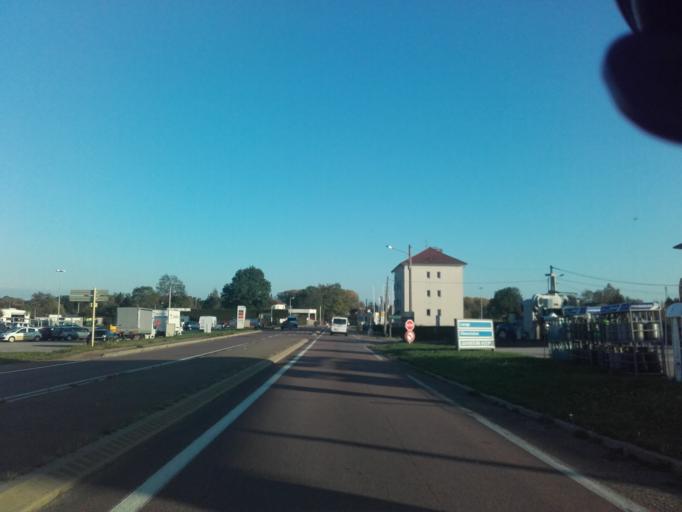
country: FR
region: Bourgogne
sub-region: Departement de la Cote-d'Or
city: Corpeau
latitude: 46.9212
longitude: 4.7485
